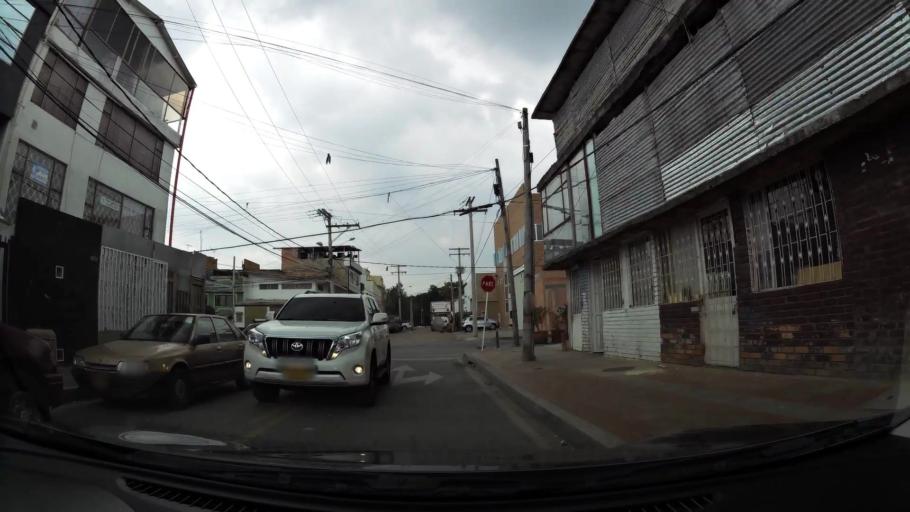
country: CO
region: Cundinamarca
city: La Calera
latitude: 4.7449
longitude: -74.0375
